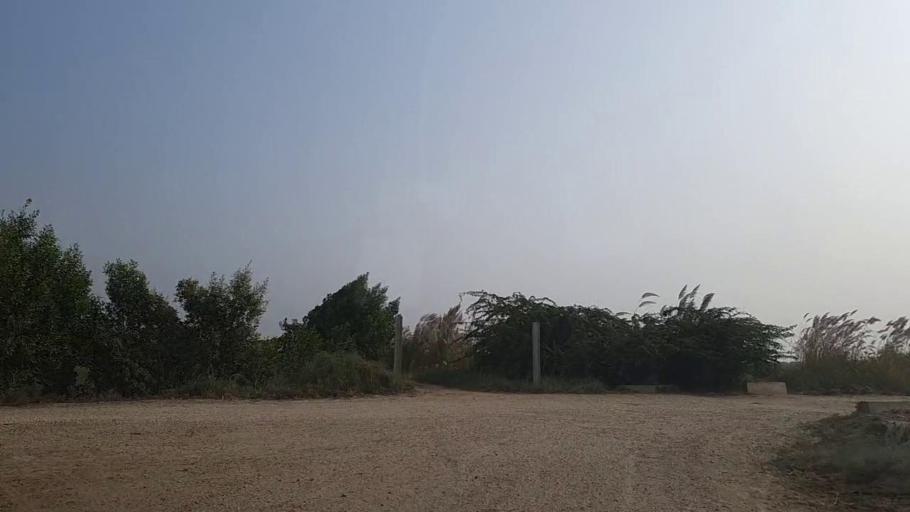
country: PK
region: Sindh
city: Gharo
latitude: 24.6500
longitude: 67.6226
